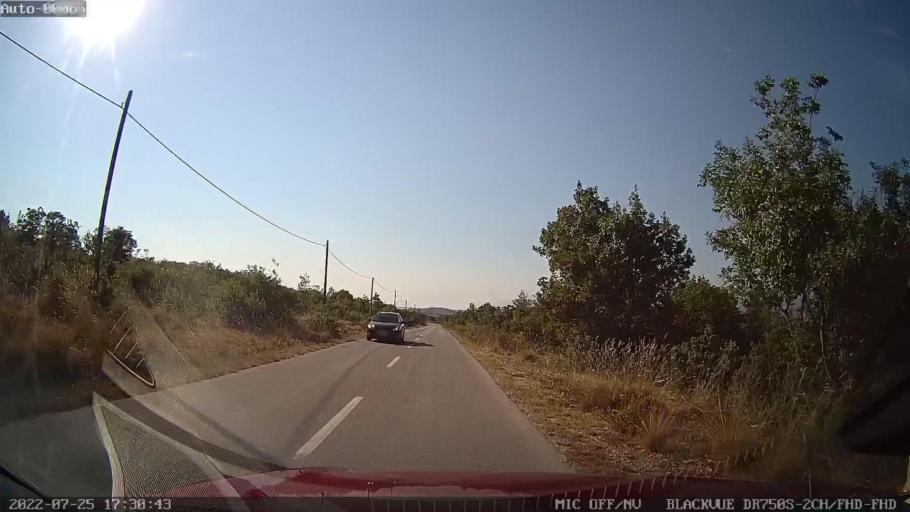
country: HR
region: Zadarska
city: Posedarje
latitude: 44.1657
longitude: 15.5059
